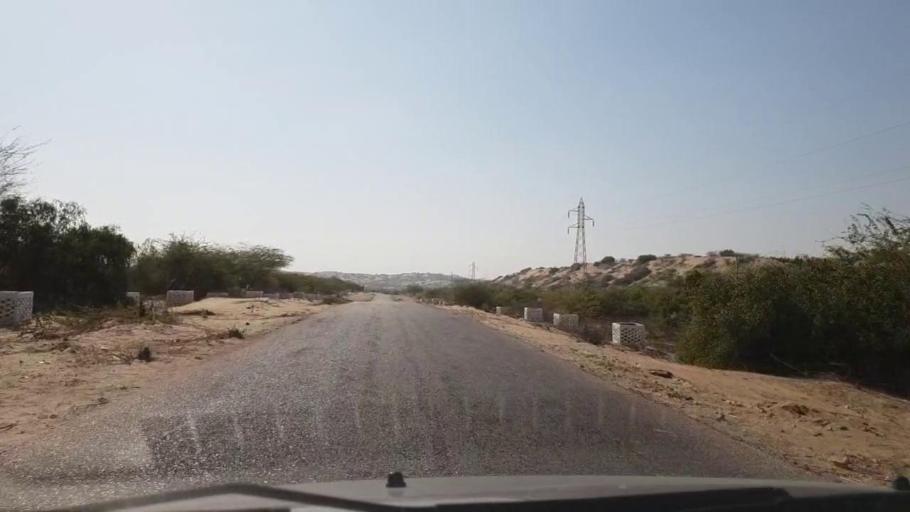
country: PK
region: Sindh
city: Diplo
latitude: 24.4863
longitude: 69.5871
